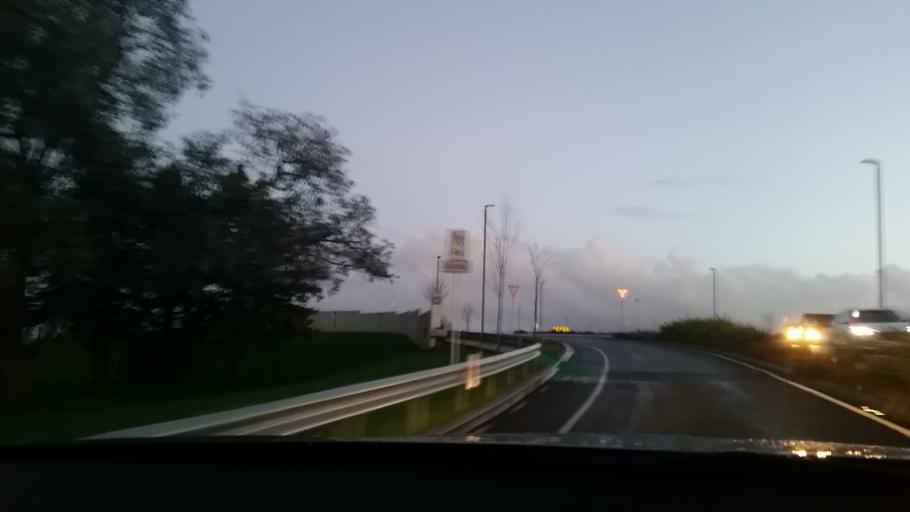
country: NZ
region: Waikato
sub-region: Hamilton City
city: Hamilton
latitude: -37.8175
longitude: 175.2268
